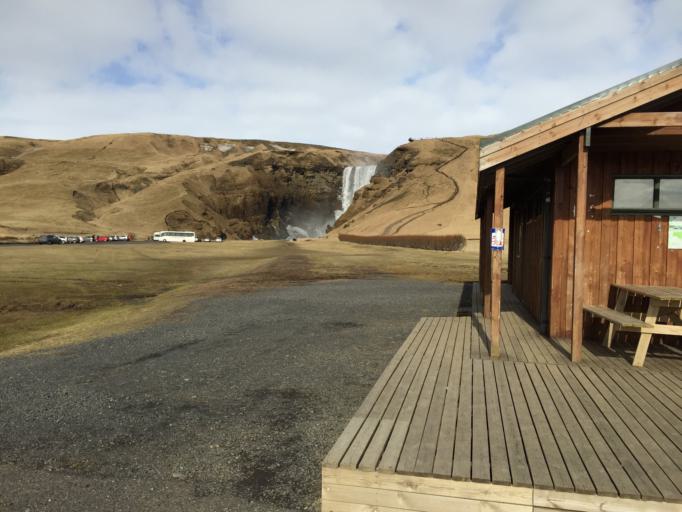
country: IS
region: South
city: Vestmannaeyjar
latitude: 63.5278
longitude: -19.5122
